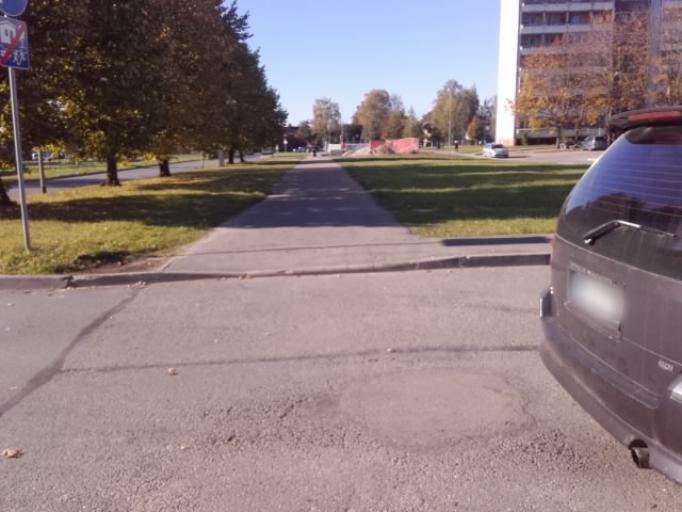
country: LV
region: Stopini
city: Ulbroka
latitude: 56.9407
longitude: 24.1980
